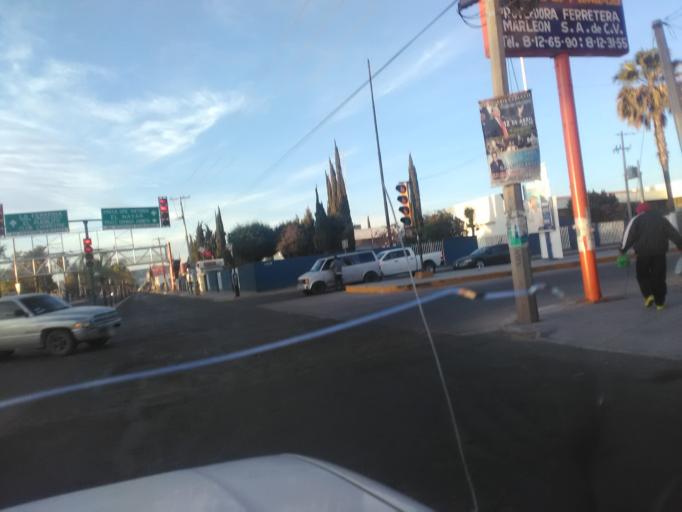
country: MX
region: Durango
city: Victoria de Durango
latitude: 23.9958
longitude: -104.6629
